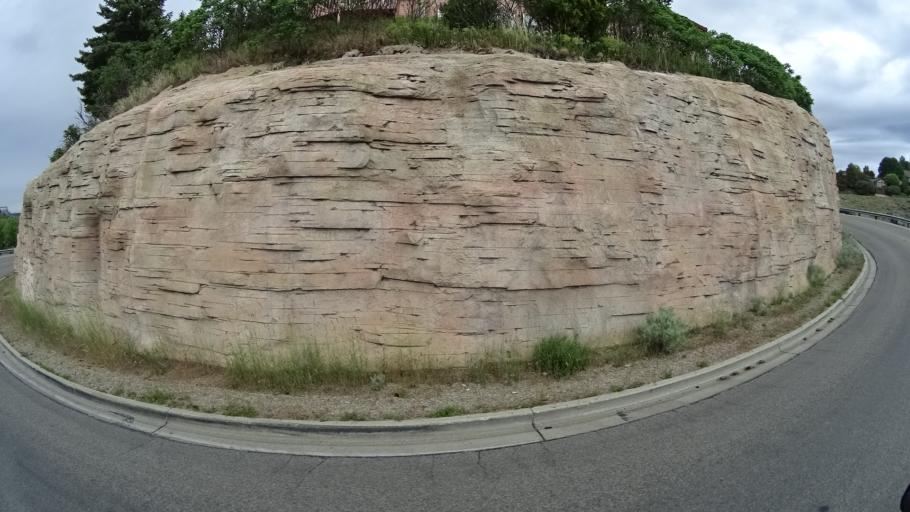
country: US
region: Idaho
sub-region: Ada County
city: Boise
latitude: 43.6148
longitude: -116.1756
